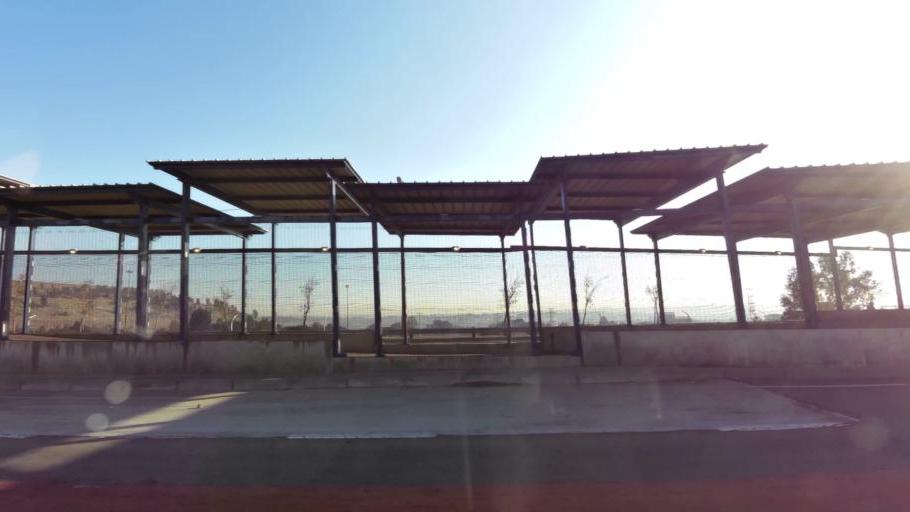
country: ZA
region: Gauteng
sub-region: City of Johannesburg Metropolitan Municipality
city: Johannesburg
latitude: -26.2315
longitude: 27.9822
